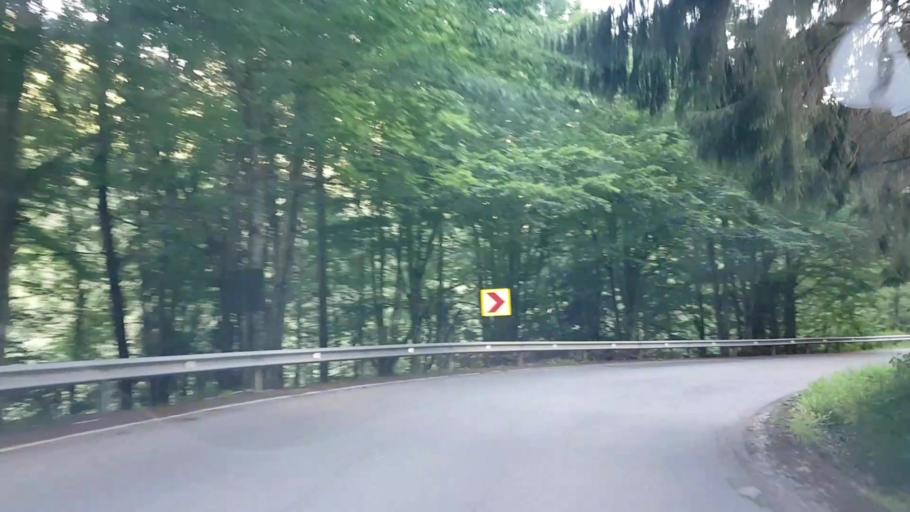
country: RO
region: Harghita
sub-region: Comuna Praid
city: Ocna de Sus
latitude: 46.5839
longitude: 25.2431
